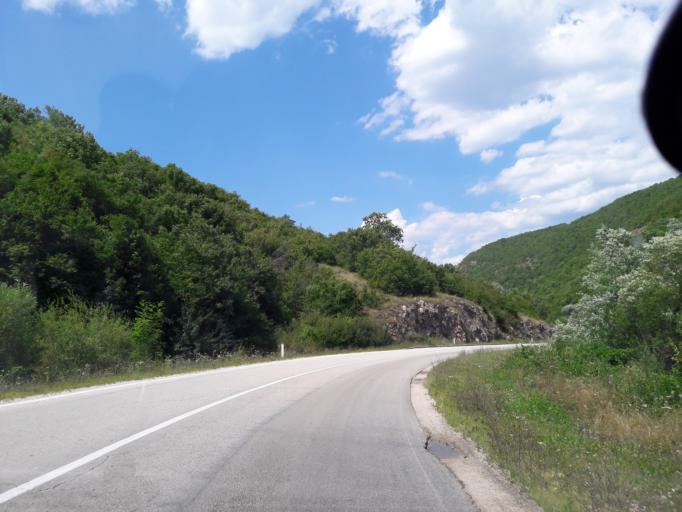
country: BA
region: Republika Srpska
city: Mrkonjic Grad
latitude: 44.4476
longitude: 17.1627
